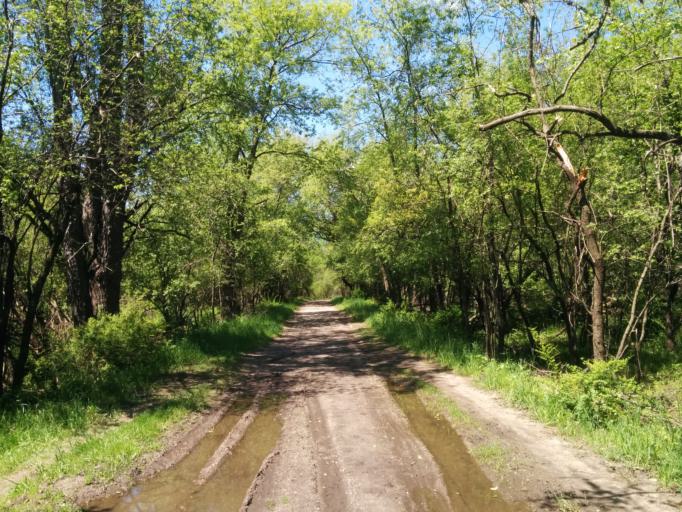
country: US
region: Illinois
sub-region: Cook County
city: Schiller Park
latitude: 41.9808
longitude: -87.8537
